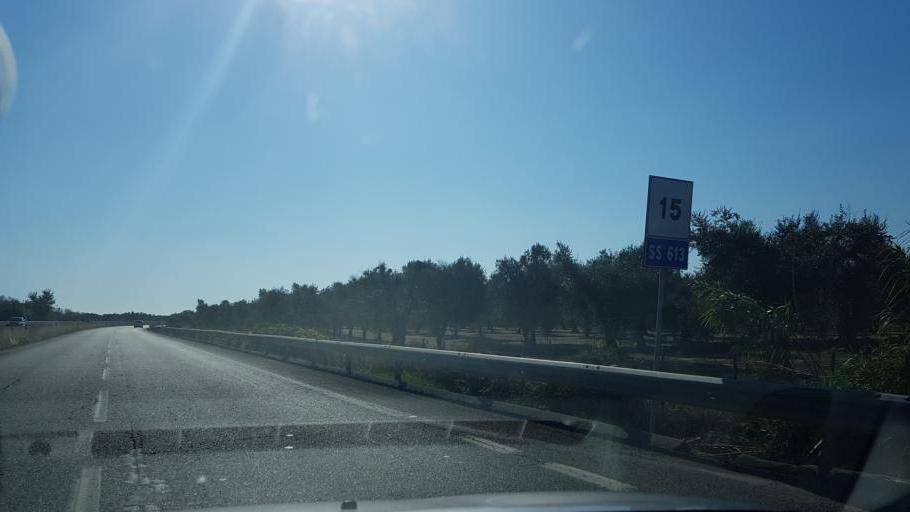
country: IT
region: Apulia
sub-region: Provincia di Brindisi
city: Torchiarolo
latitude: 40.5022
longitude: 18.0288
